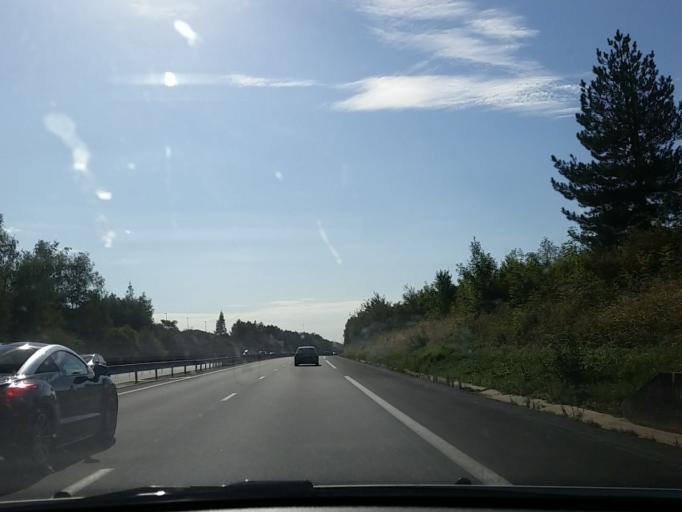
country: FR
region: Centre
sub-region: Departement du Cher
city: Vierzon
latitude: 47.2363
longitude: 2.0896
